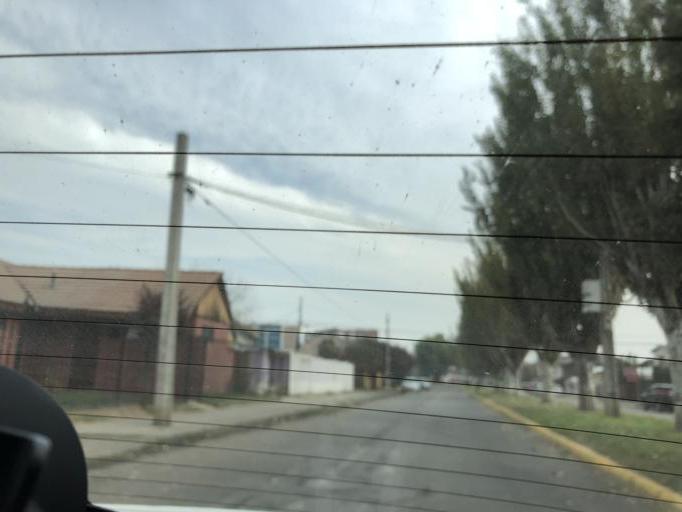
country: CL
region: Santiago Metropolitan
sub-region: Provincia de Cordillera
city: Puente Alto
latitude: -33.5573
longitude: -70.5578
